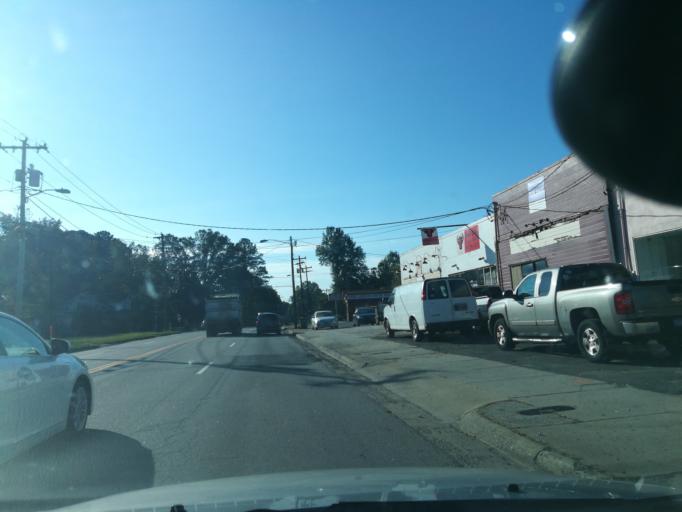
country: US
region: North Carolina
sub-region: Durham County
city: Durham
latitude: 36.0278
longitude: -78.8900
